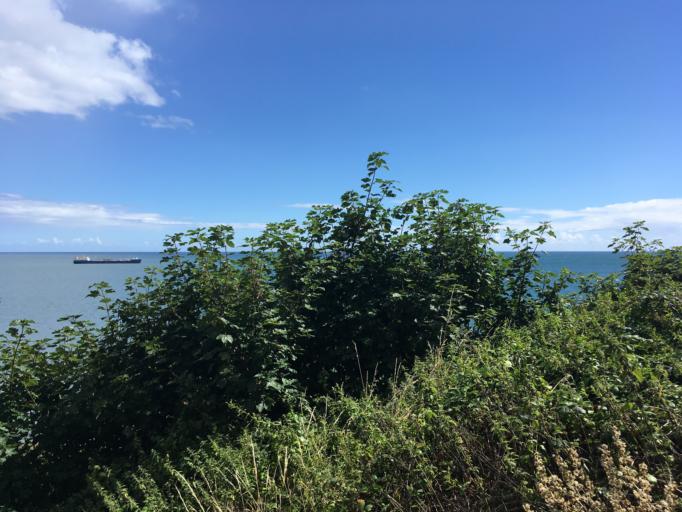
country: IE
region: Munster
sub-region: County Cork
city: Crosshaven
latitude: 51.7803
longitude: -8.2937
